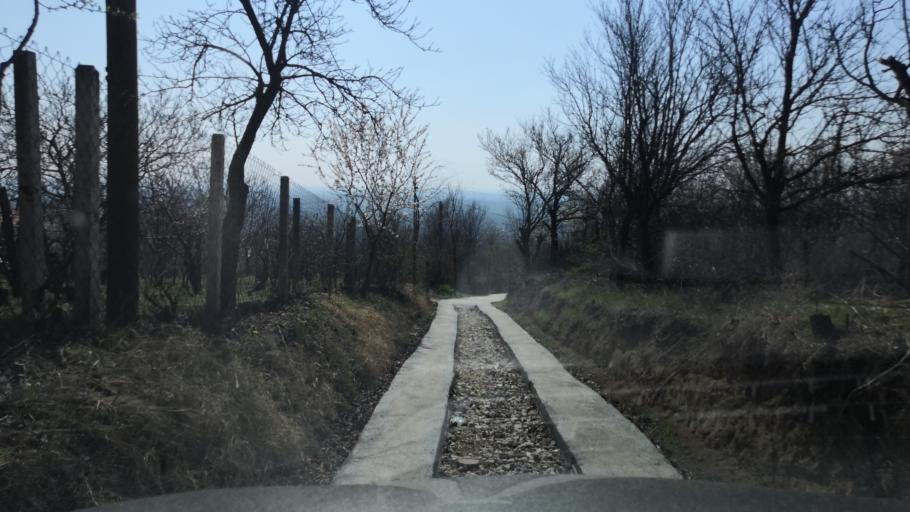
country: RS
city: Krcedin
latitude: 45.1607
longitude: 20.1866
